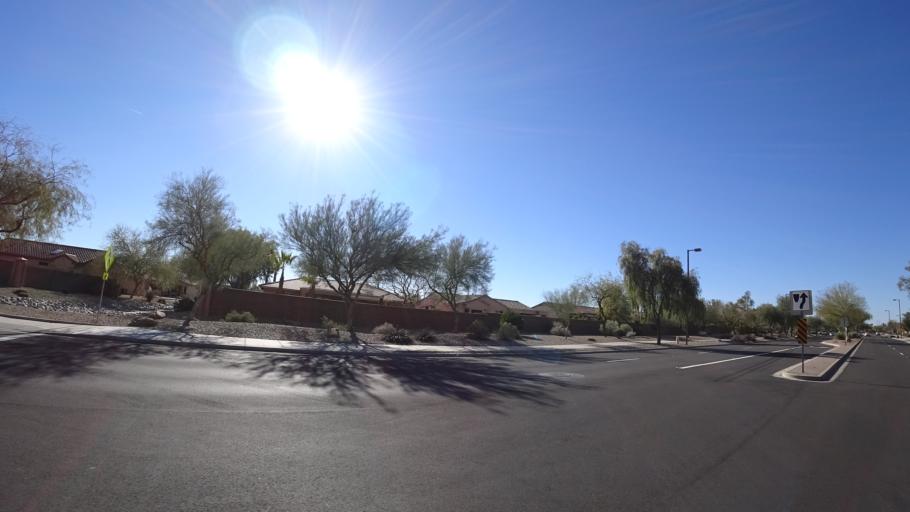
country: US
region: Arizona
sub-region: Maricopa County
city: Sun City West
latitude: 33.6560
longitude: -112.3811
